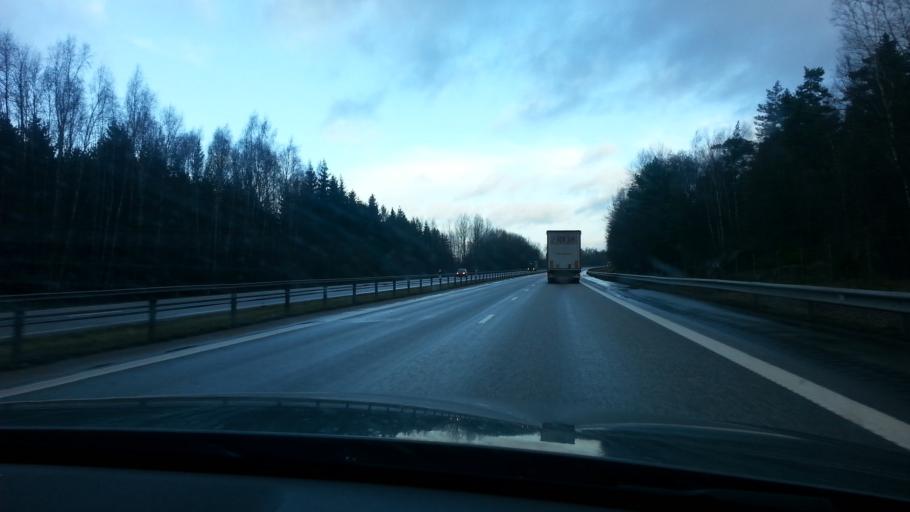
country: SE
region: OEstergoetland
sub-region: Odeshogs Kommun
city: OEdeshoeg
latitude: 58.1652
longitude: 14.5830
